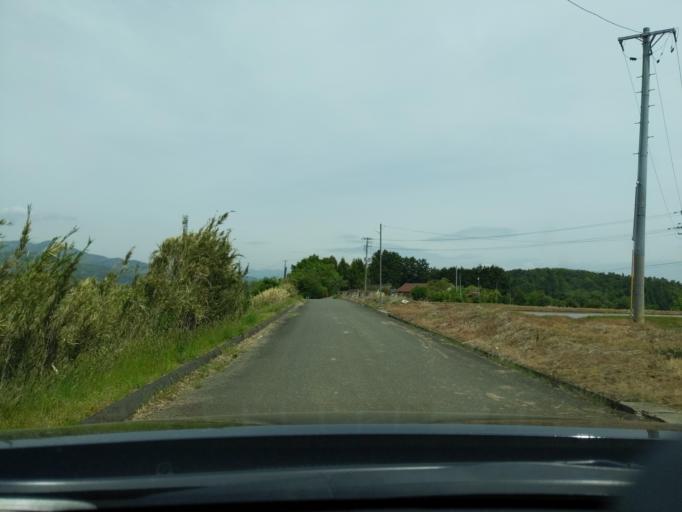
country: JP
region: Fukushima
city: Koriyama
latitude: 37.4019
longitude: 140.2895
